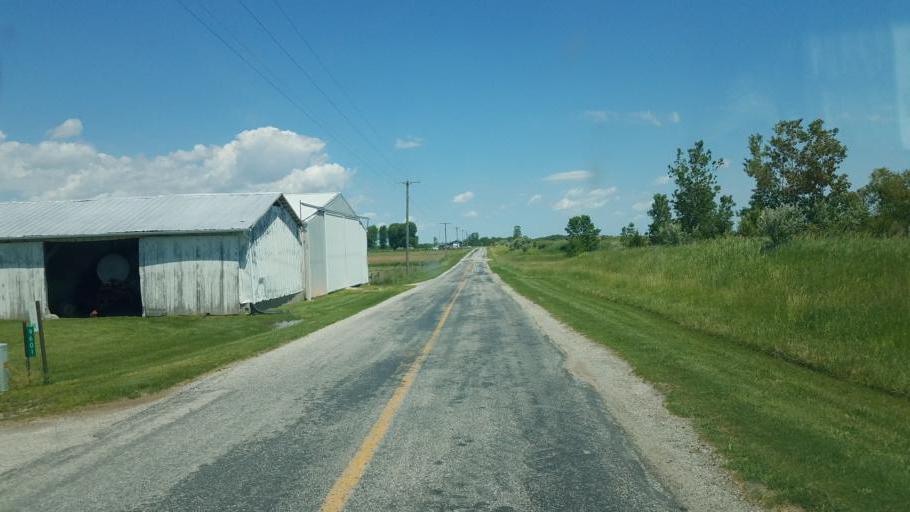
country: US
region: Ohio
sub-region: Hardin County
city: Forest
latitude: 40.6782
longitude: -83.4197
